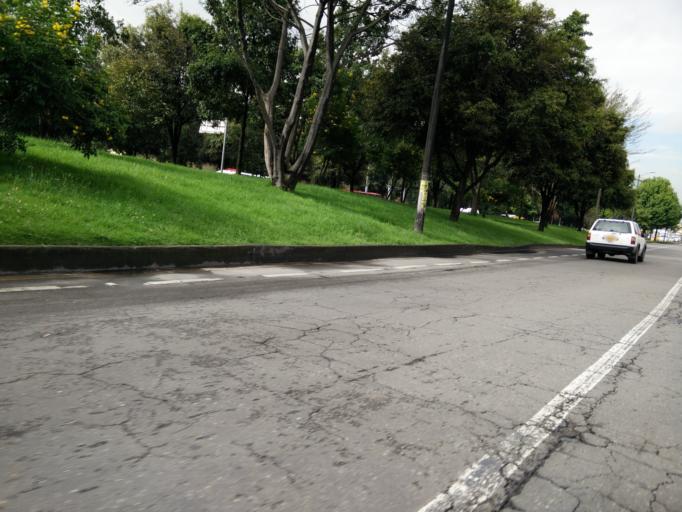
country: CO
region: Bogota D.C.
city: Bogota
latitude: 4.6654
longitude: -74.1073
